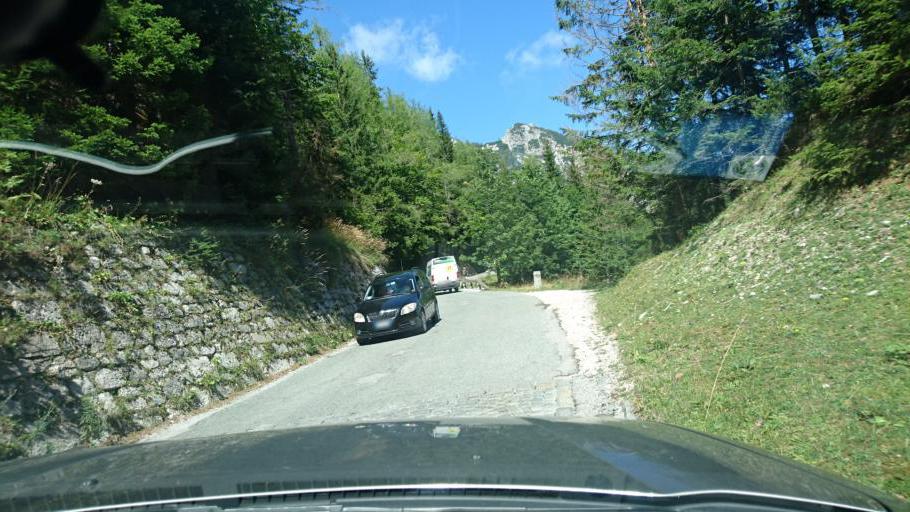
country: SI
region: Kranjska Gora
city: Kranjska Gora
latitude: 46.4389
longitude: 13.7604
